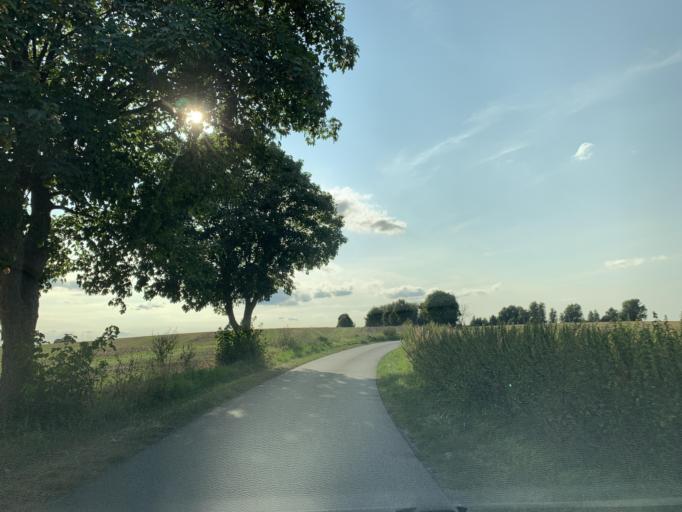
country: DE
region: Mecklenburg-Vorpommern
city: Loitz
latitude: 53.3538
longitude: 13.3859
